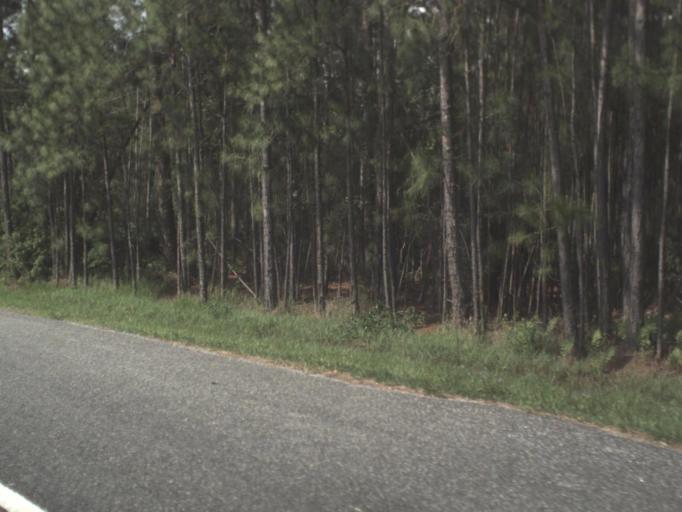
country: US
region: Florida
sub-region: Saint Johns County
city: Saint Augustine Shores
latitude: 29.7815
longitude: -81.3172
